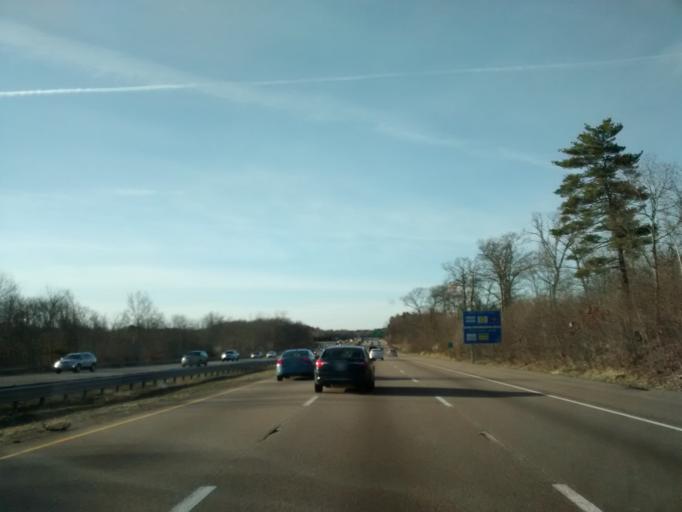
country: US
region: Massachusetts
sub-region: Norfolk County
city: Randolph
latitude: 42.1492
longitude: -71.0671
